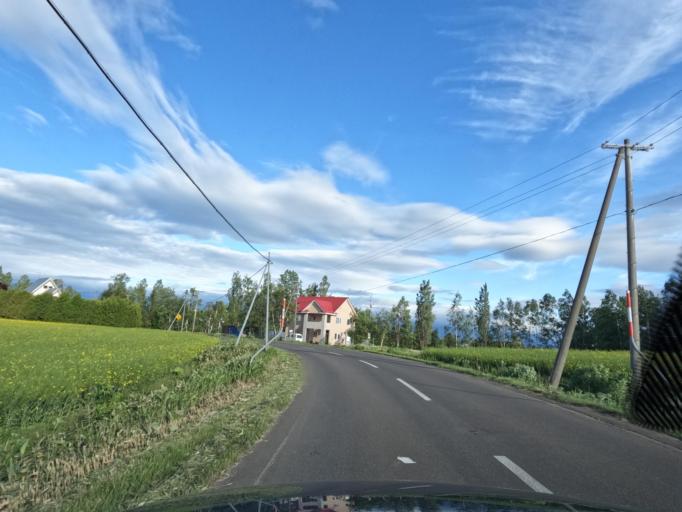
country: JP
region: Hokkaido
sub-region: Asahikawa-shi
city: Asahikawa
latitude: 43.6065
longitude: 142.4607
